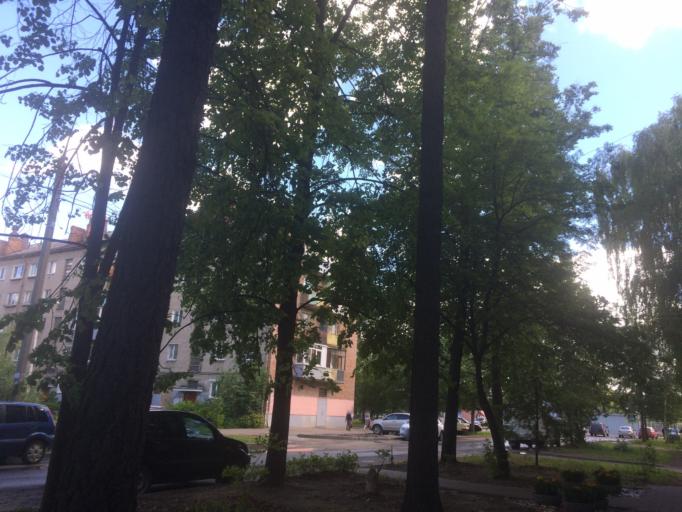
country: RU
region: Jaroslavl
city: Yaroslavl
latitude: 57.6290
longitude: 39.8621
